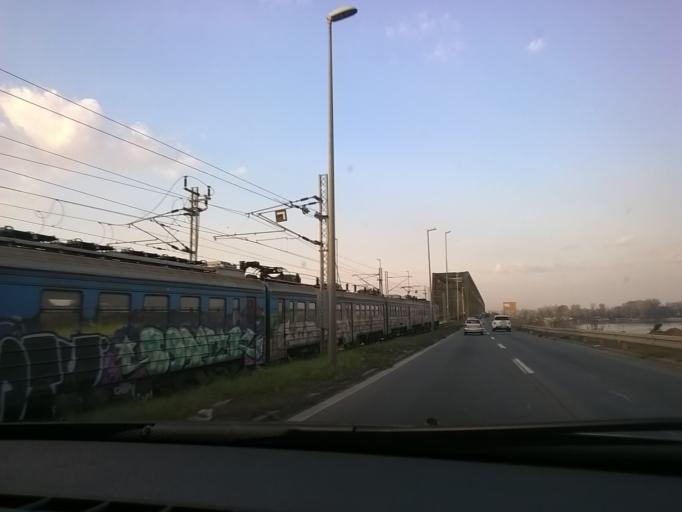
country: RS
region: Central Serbia
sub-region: Belgrade
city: Palilula
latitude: 44.8231
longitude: 20.4911
